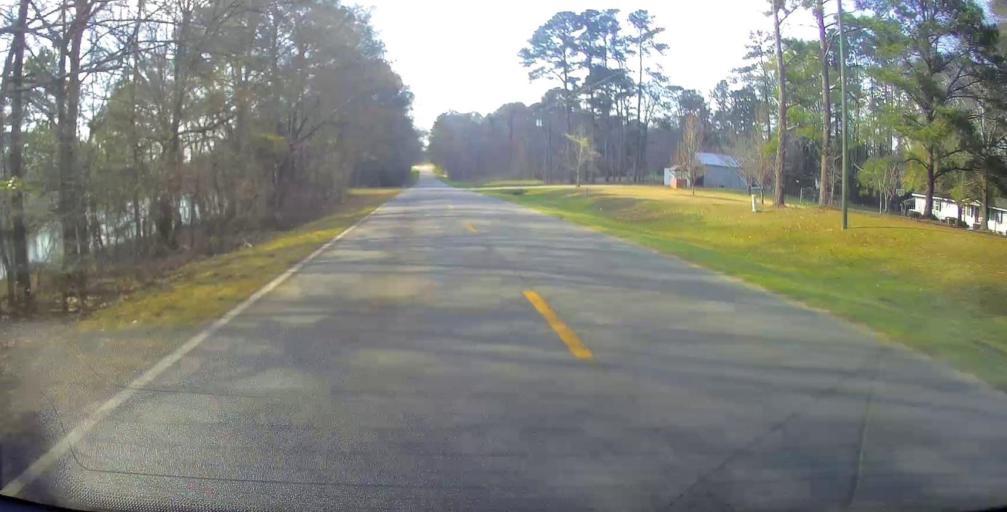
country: US
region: Georgia
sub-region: Laurens County
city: Dublin
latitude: 32.5665
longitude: -83.0271
